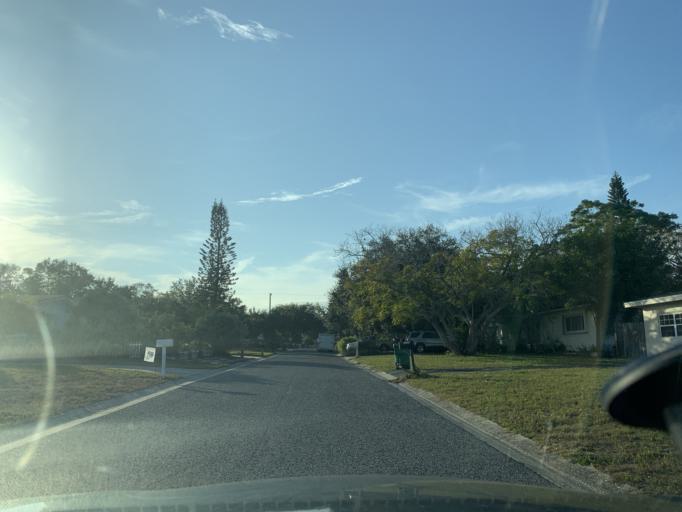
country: US
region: Florida
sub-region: Pinellas County
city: Ridgecrest
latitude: 27.8817
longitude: -82.7968
